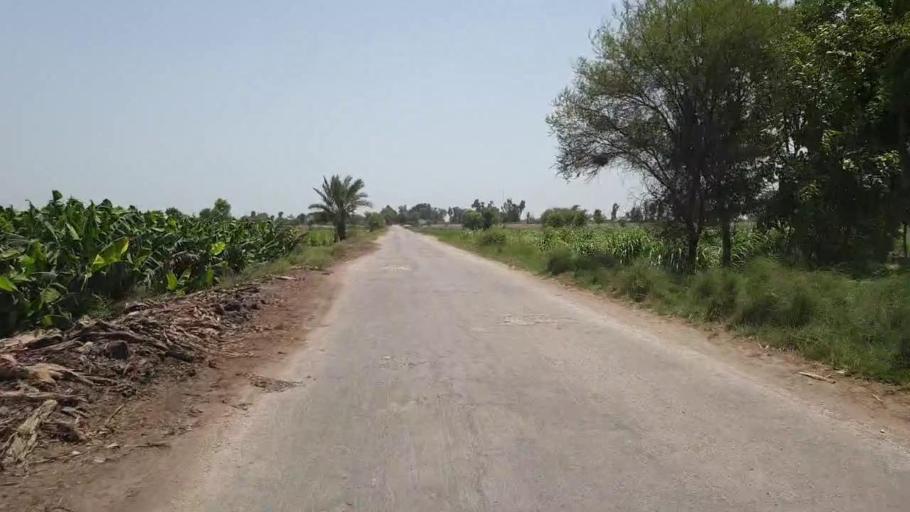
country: PK
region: Sindh
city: Daur
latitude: 26.3793
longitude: 68.1711
